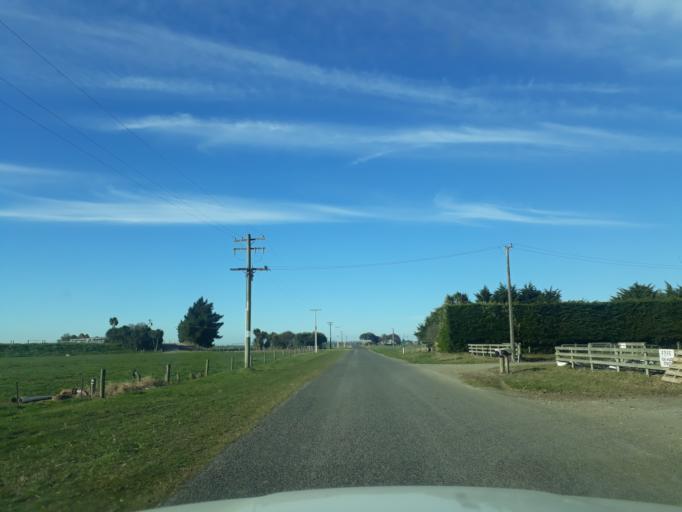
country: NZ
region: Canterbury
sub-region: Timaru District
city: Timaru
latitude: -44.2708
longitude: 171.3441
